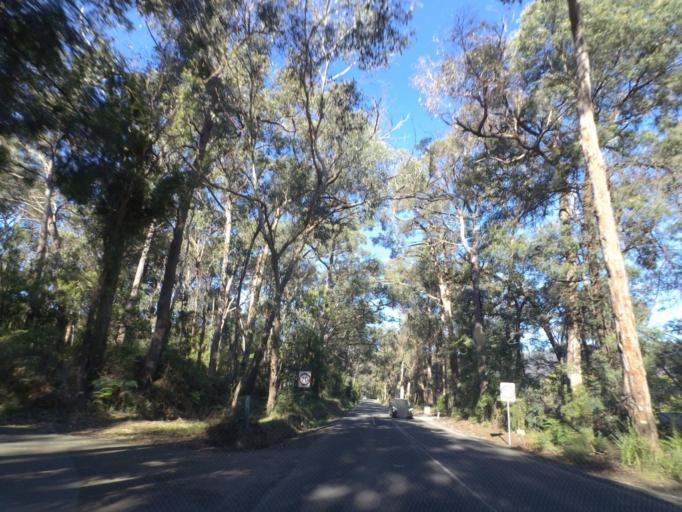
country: AU
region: Victoria
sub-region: Yarra Ranges
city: Montrose
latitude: -37.8030
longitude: 145.3455
